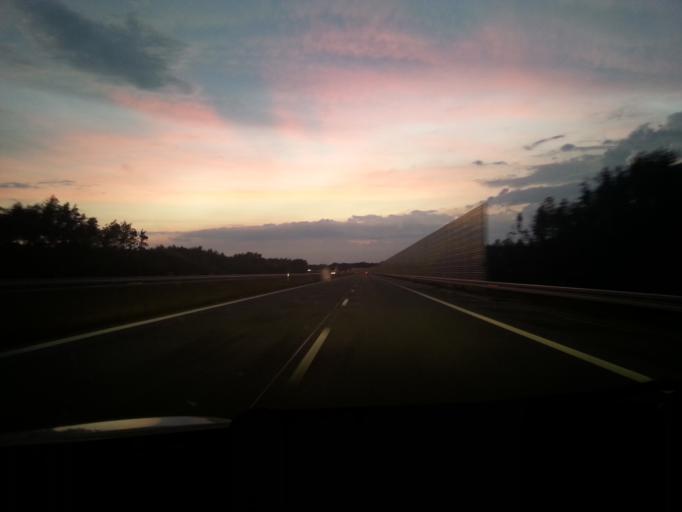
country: PL
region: Lodz Voivodeship
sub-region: Powiat zdunskowolski
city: Zdunska Wola
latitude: 51.5879
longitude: 18.8958
